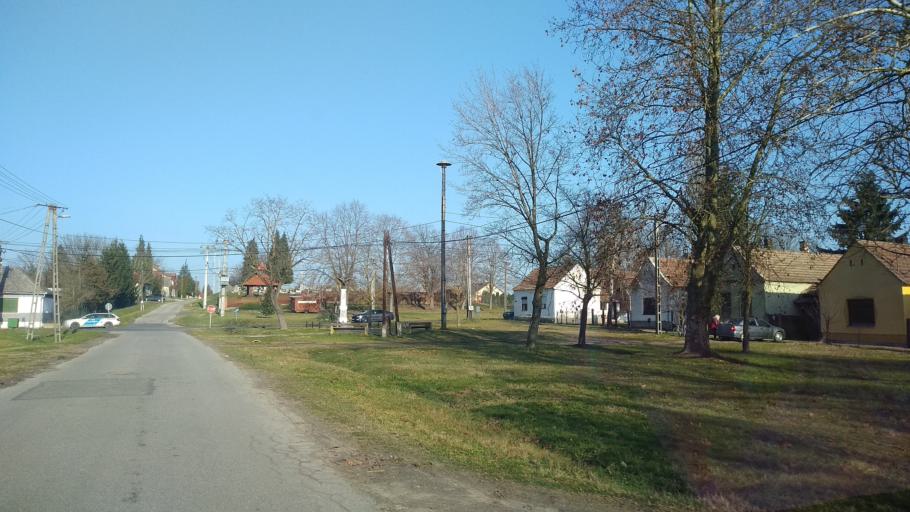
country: HU
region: Somogy
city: Barcs
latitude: 45.9612
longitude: 17.4855
